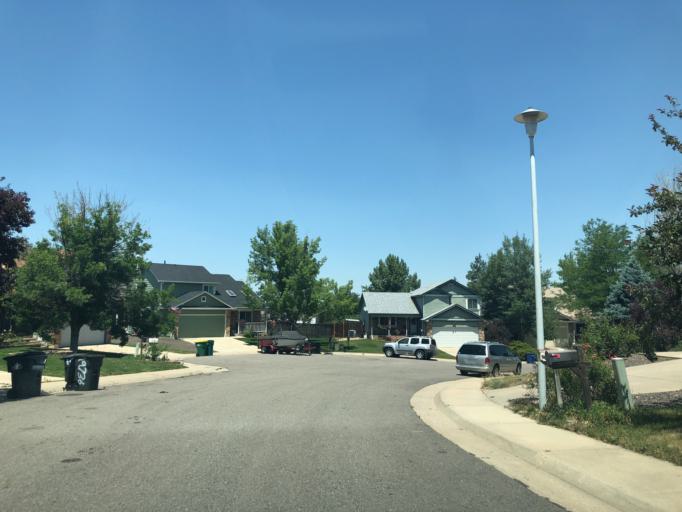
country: US
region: Colorado
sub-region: Arapahoe County
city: Dove Valley
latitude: 39.6256
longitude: -104.7584
